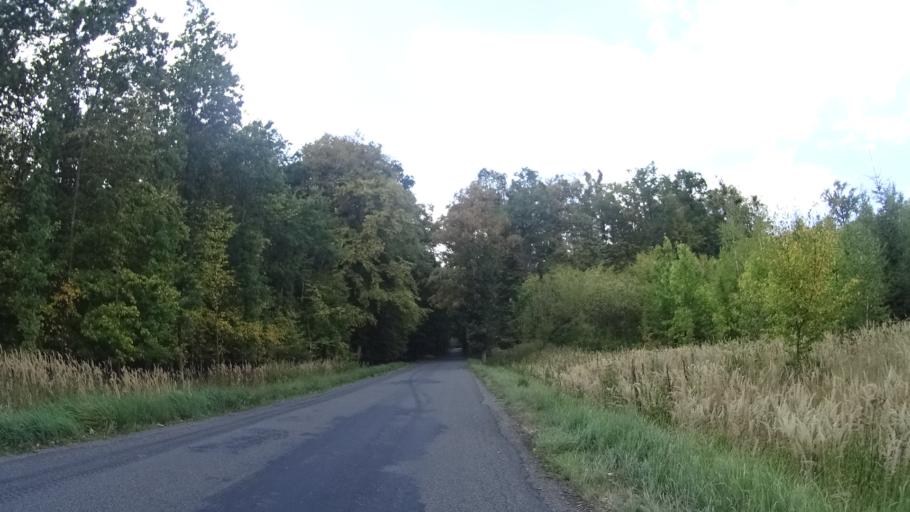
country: CZ
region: Olomoucky
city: Bila Lhota
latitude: 49.7280
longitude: 17.0141
